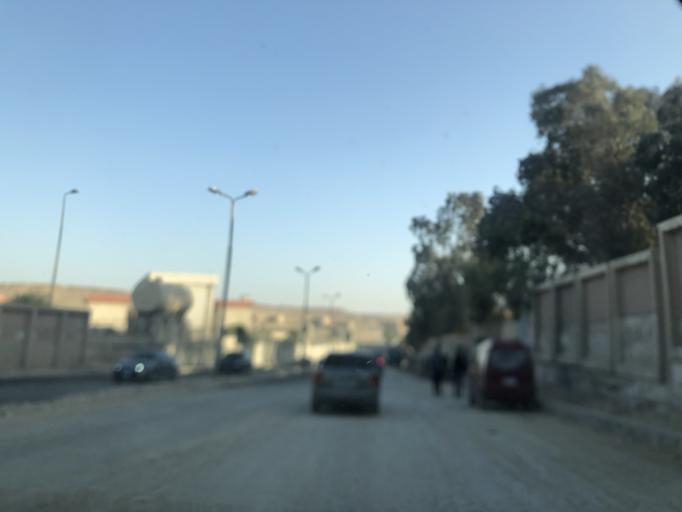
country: EG
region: Al Jizah
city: Al Jizah
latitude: 29.9822
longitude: 31.1127
